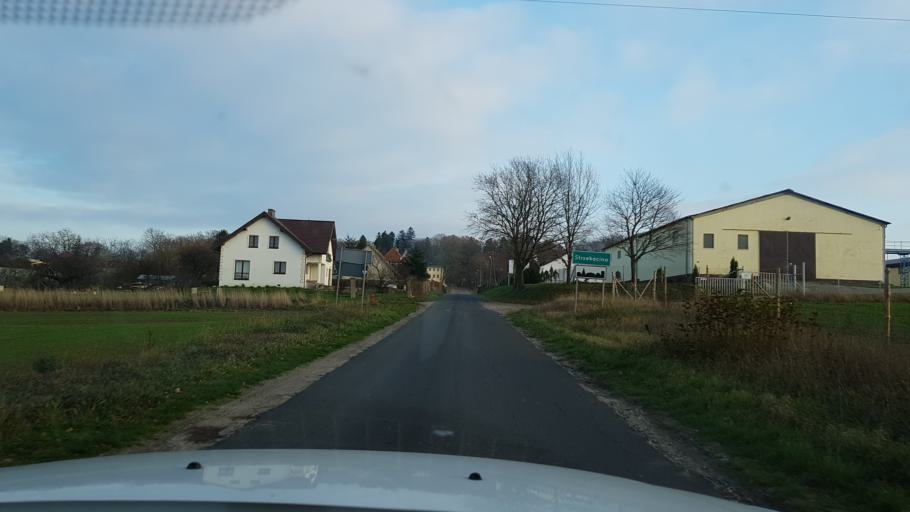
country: PL
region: West Pomeranian Voivodeship
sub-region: Koszalin
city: Koszalin
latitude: 54.1015
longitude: 16.1527
